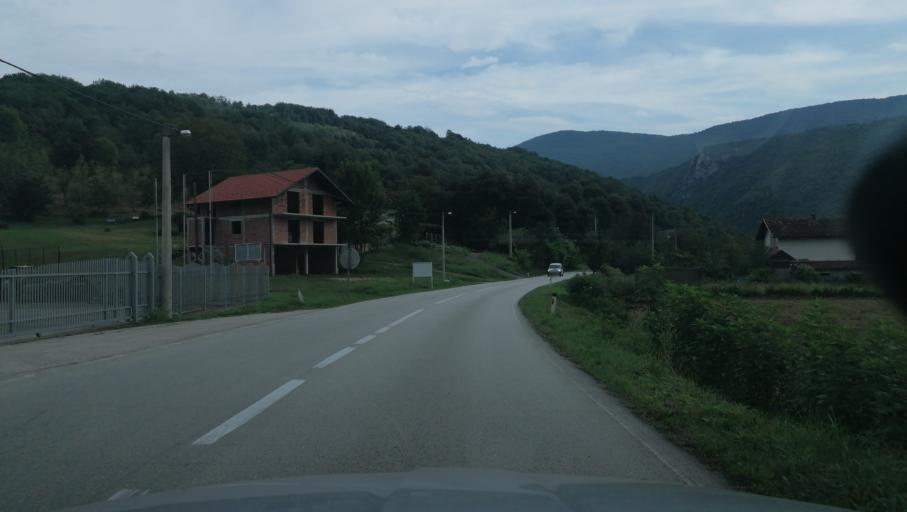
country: BA
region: Republika Srpska
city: Hiseti
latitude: 44.6200
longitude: 17.1457
